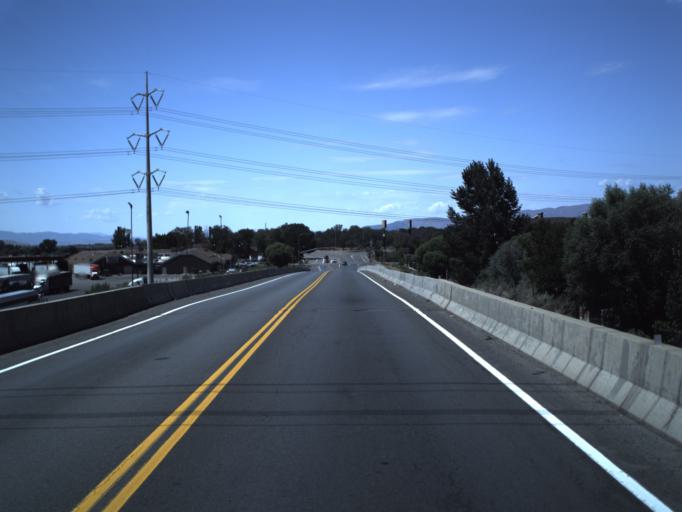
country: US
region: Utah
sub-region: Utah County
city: Springville
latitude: 40.1882
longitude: -111.6381
